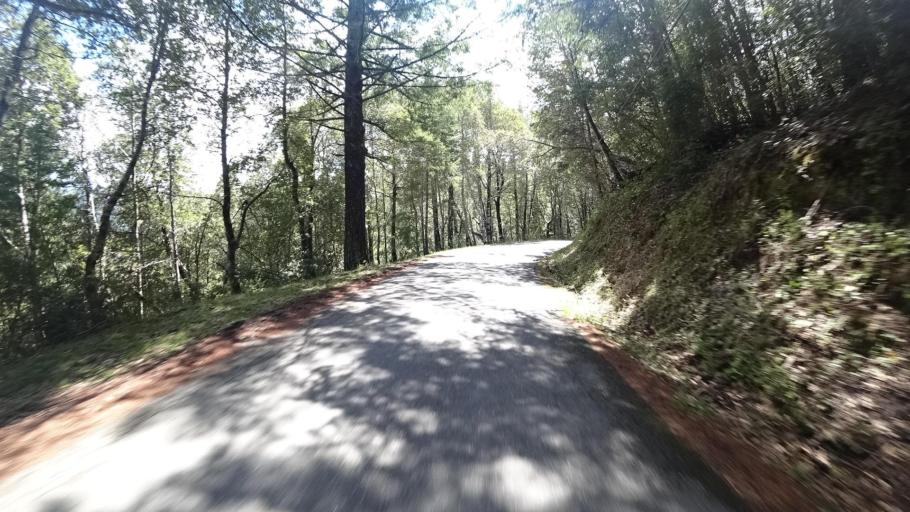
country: US
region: California
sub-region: Humboldt County
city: Blue Lake
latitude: 40.7616
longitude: -123.9497
